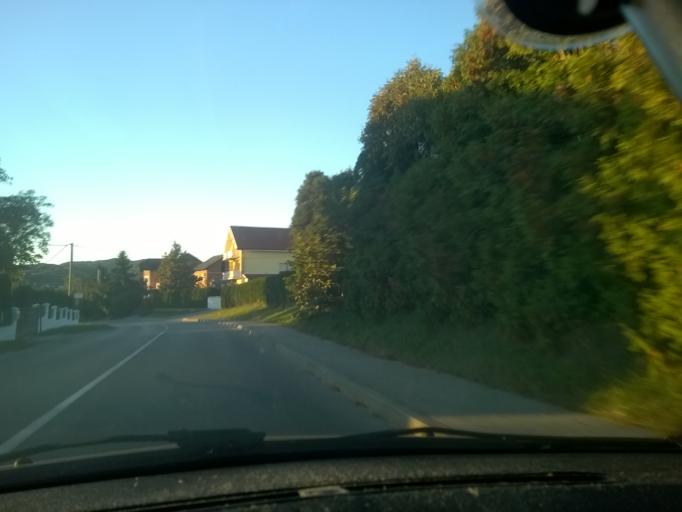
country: HR
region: Krapinsko-Zagorska
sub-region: Grad Krapina
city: Krapina
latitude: 46.1359
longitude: 15.8835
